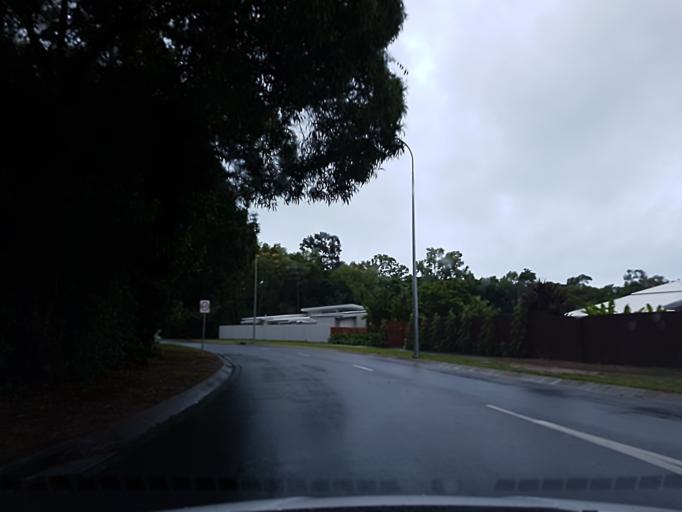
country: AU
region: Queensland
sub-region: Cairns
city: Palm Cove
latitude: -16.7549
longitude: 145.6650
